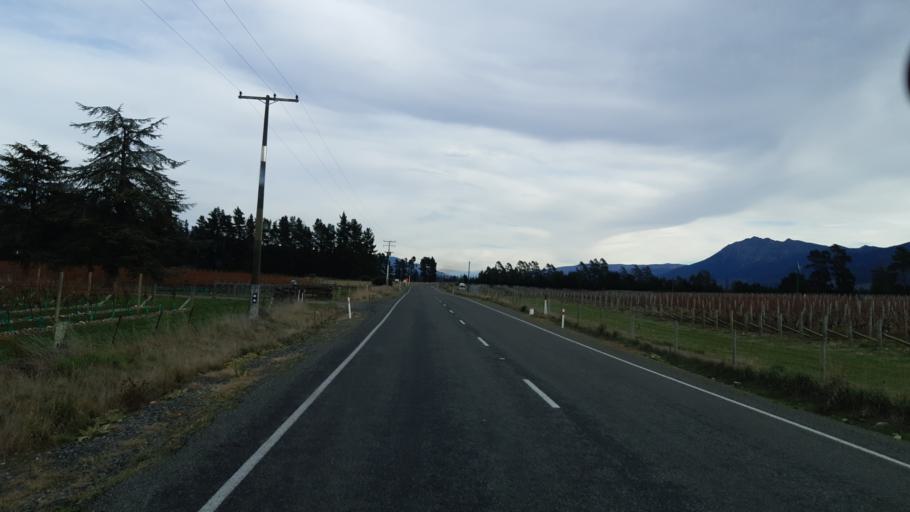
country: NZ
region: Nelson
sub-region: Nelson City
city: Nelson
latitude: -41.6016
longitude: 173.4215
